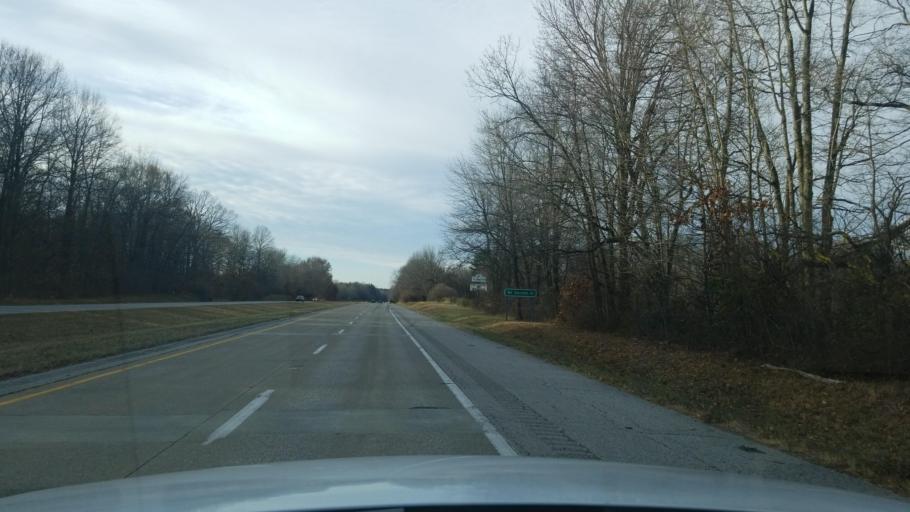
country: US
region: Indiana
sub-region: Vanderburgh County
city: Evansville
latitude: 37.9626
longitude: -87.6900
